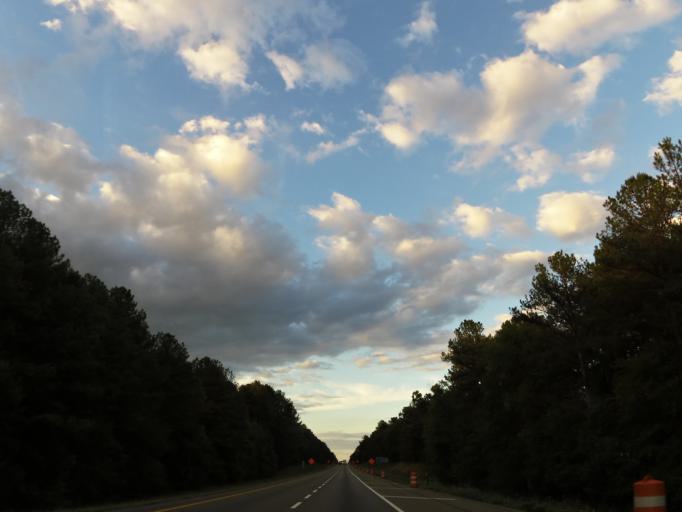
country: US
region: Tennessee
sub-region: Bradley County
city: Hopewell
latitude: 35.2598
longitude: -84.8326
